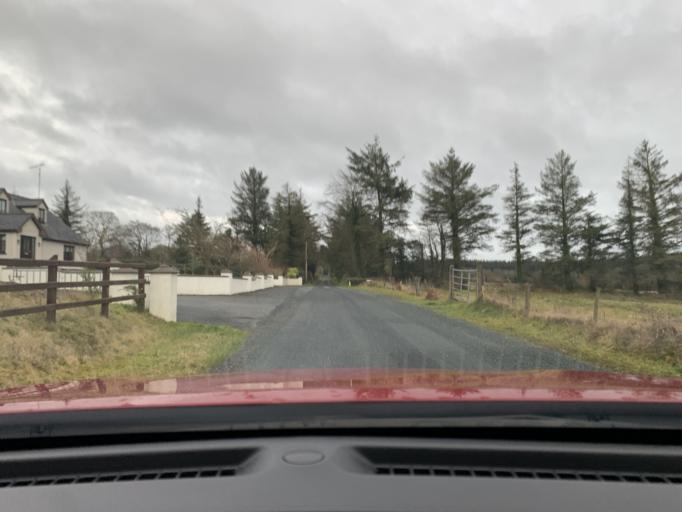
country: IE
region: Connaught
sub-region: Roscommon
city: Ballaghaderreen
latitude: 53.9662
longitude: -8.5140
